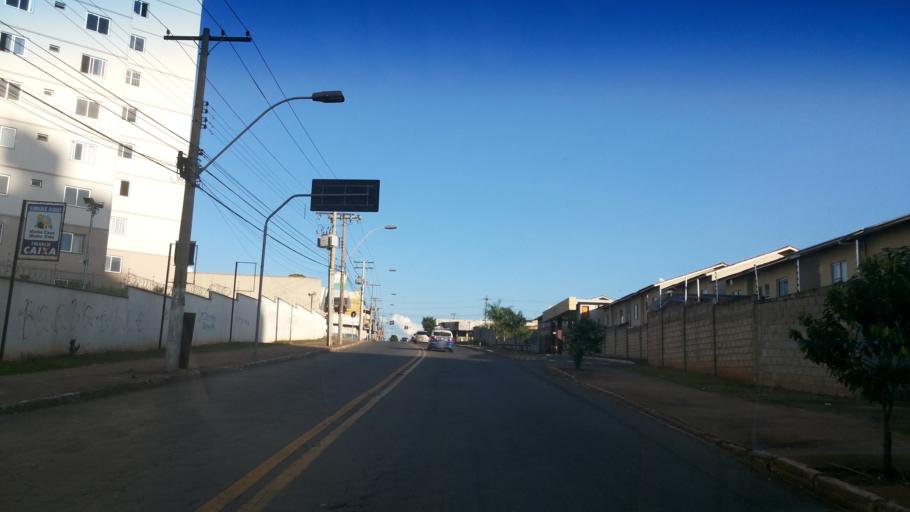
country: BR
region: Goias
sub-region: Goiania
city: Goiania
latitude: -16.6521
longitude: -49.2735
